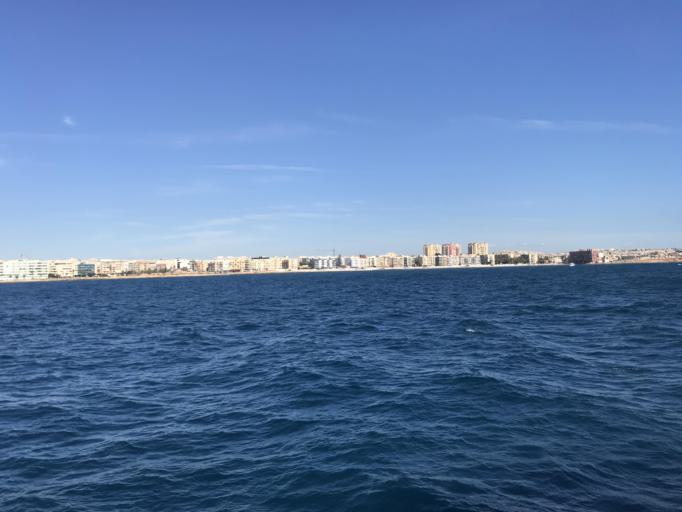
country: ES
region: Valencia
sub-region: Provincia de Alicante
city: Torrevieja
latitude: 37.9733
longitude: -0.6585
